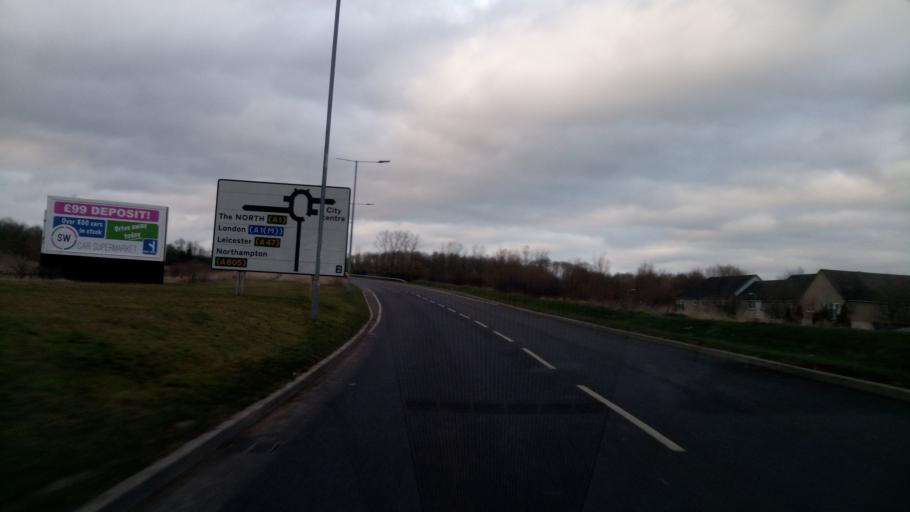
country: GB
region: England
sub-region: Cambridgeshire
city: Yaxley
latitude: 52.5386
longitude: -0.2811
